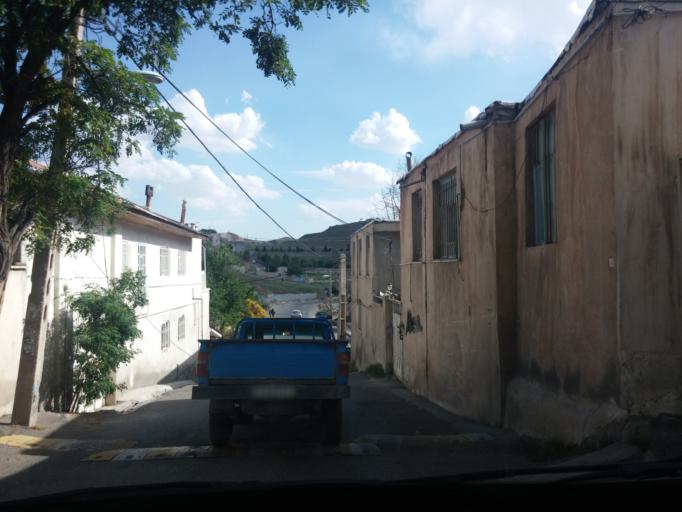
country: IR
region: Tehran
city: Damavand
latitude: 35.7303
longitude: 51.9064
